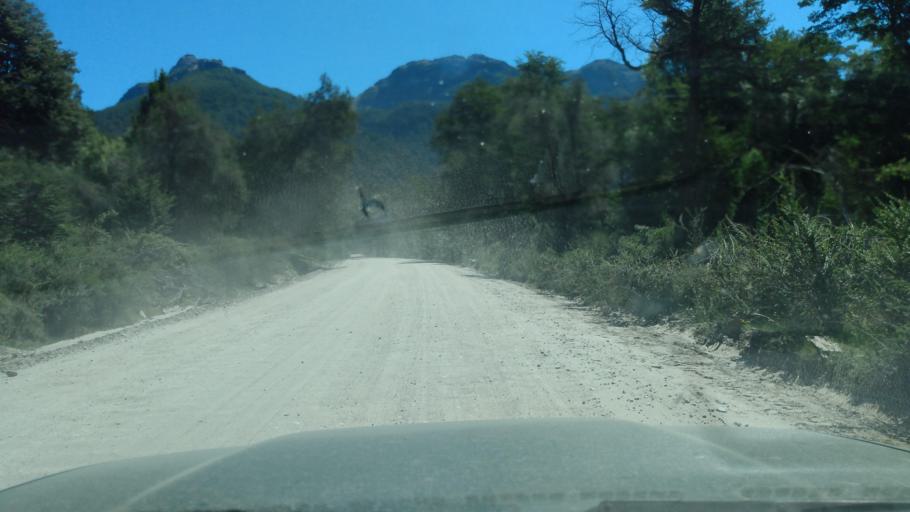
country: AR
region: Neuquen
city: Villa La Angostura
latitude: -40.6236
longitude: -71.5820
